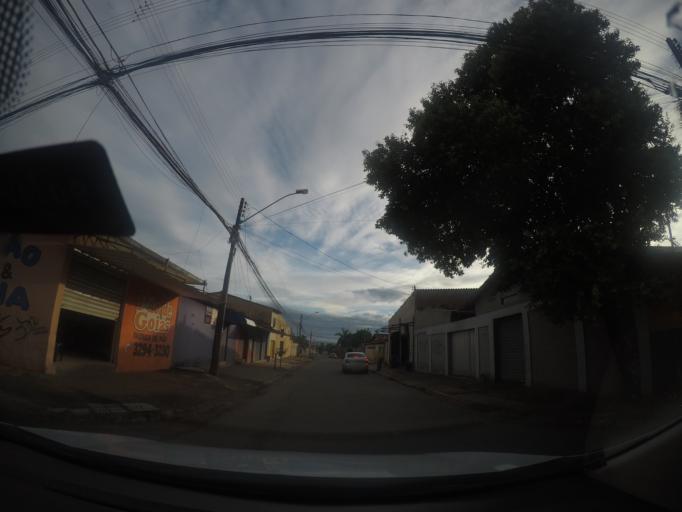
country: BR
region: Goias
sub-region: Goiania
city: Goiania
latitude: -16.6450
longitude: -49.3222
